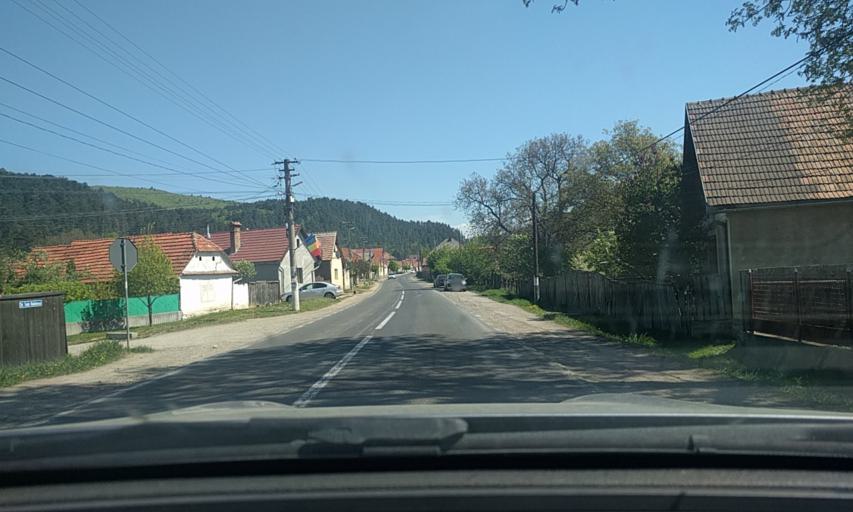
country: RO
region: Brasov
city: Tunelu-Teliu
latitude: 45.7029
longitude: 25.8473
